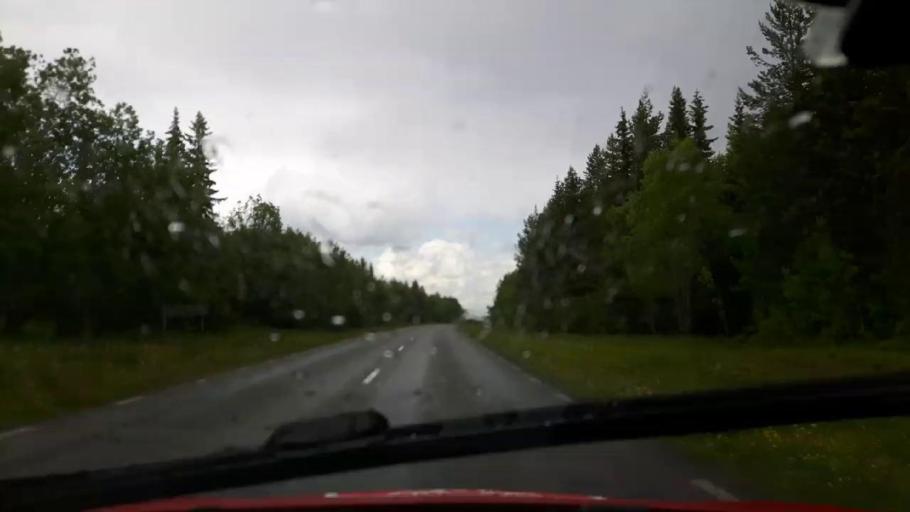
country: SE
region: Jaemtland
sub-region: Krokoms Kommun
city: Krokom
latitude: 63.4618
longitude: 14.1914
